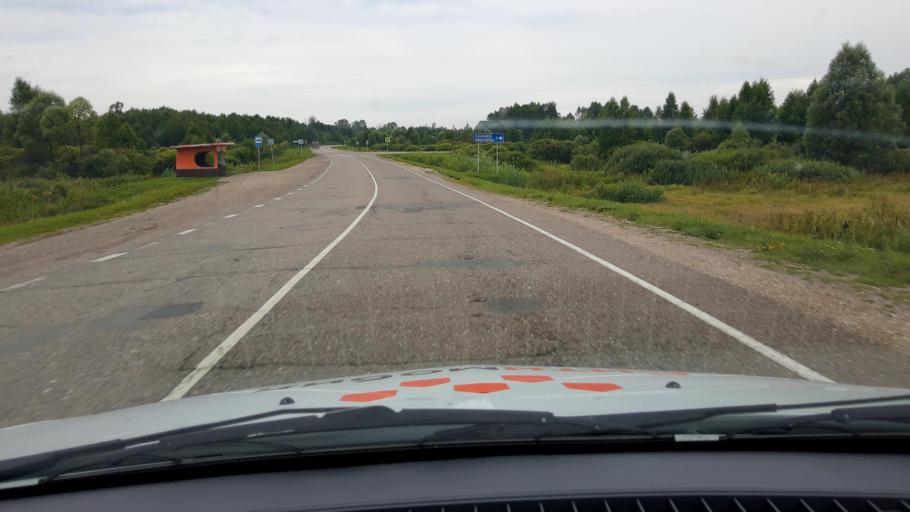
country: RU
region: Bashkortostan
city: Krasnaya Gorka
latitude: 55.1568
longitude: 56.6776
